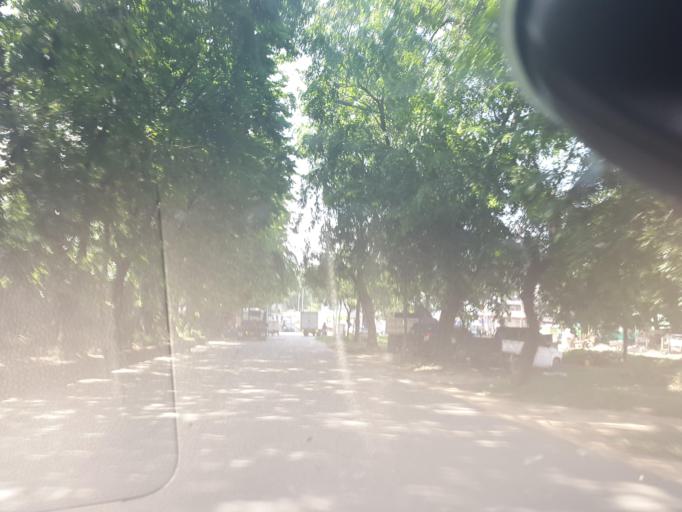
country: SG
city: Singapore
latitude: 1.1679
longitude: 104.0117
